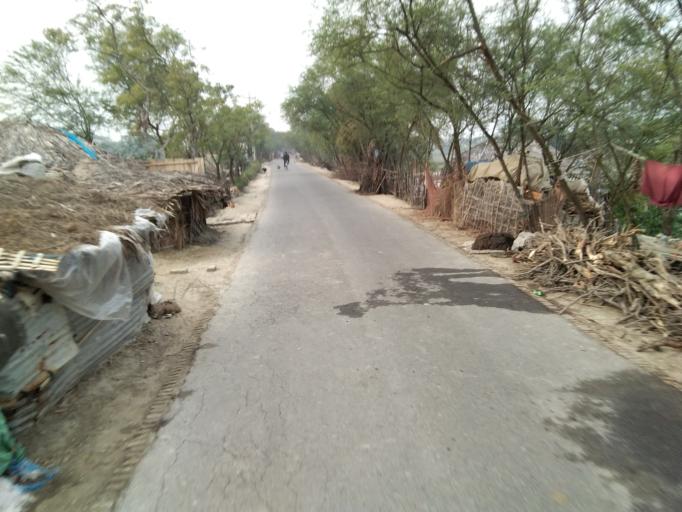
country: BD
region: Khulna
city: Satkhira
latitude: 22.5810
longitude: 89.0684
